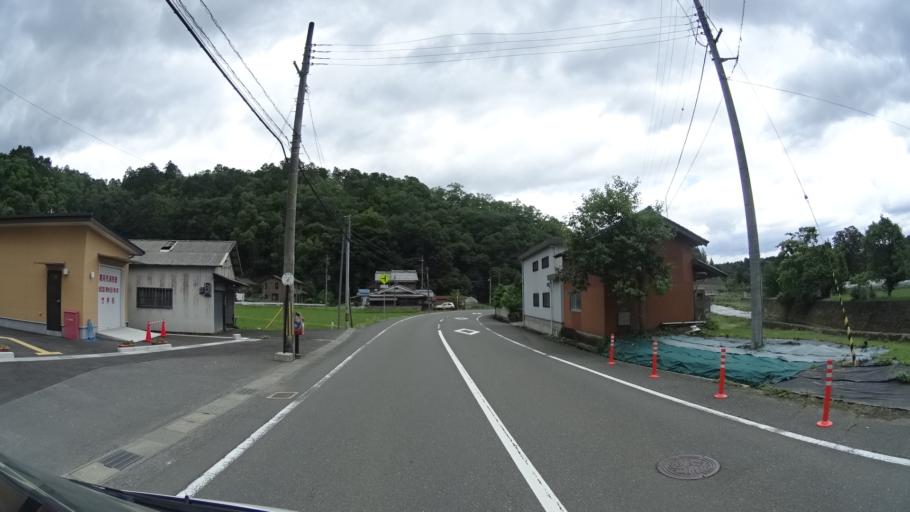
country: JP
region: Kyoto
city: Kameoka
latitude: 35.0919
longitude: 135.4214
